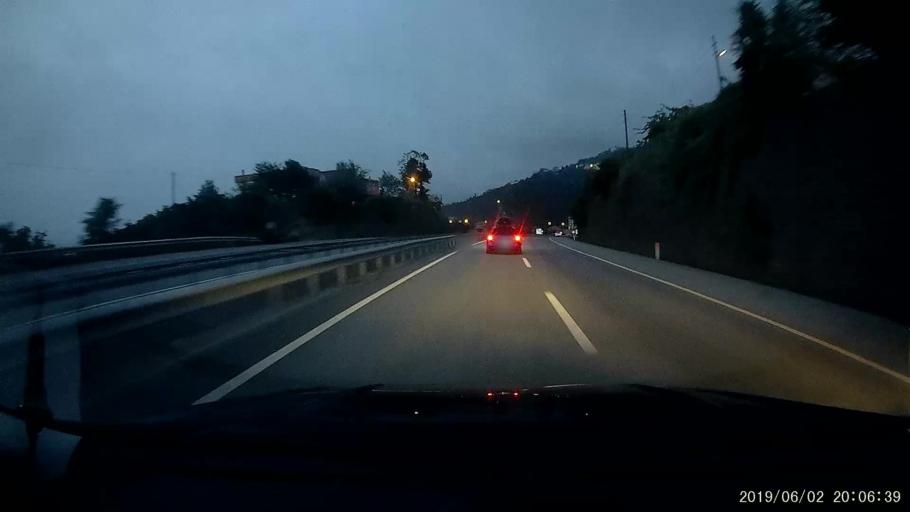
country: TR
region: Giresun
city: Gorele
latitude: 41.0362
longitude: 38.9596
